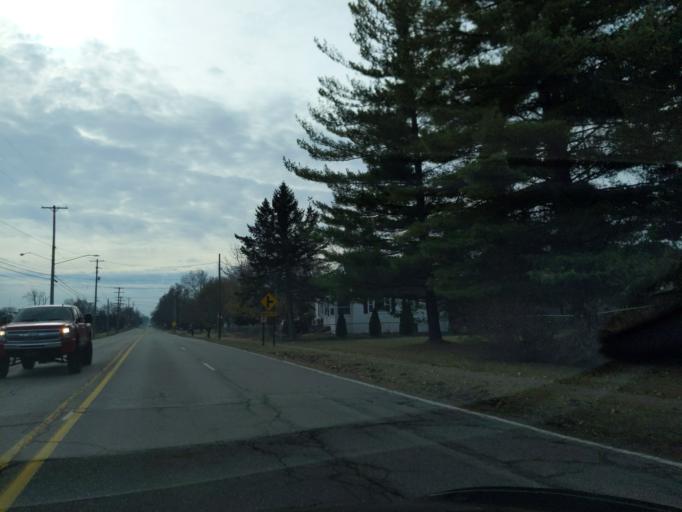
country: US
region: Michigan
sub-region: Ingham County
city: Holt
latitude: 42.6345
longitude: -84.5234
